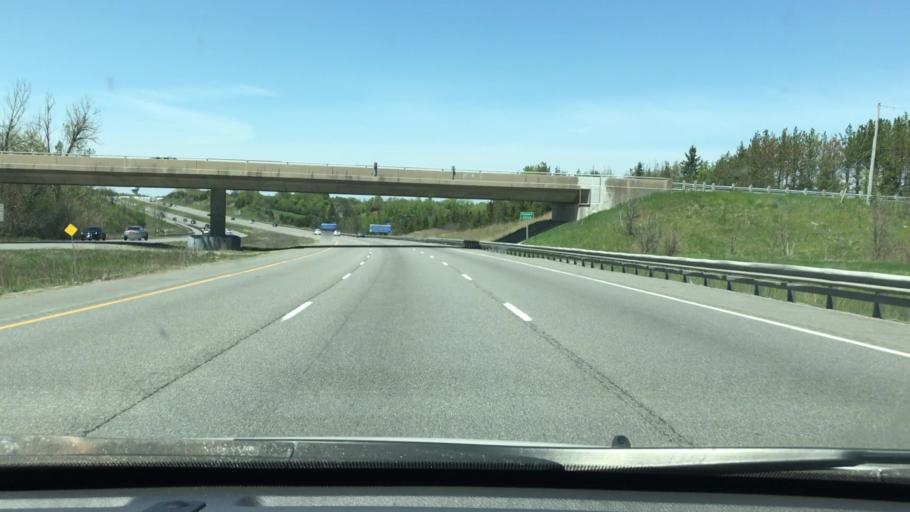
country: CA
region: Ontario
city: Newmarket
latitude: 43.9957
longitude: -79.3961
